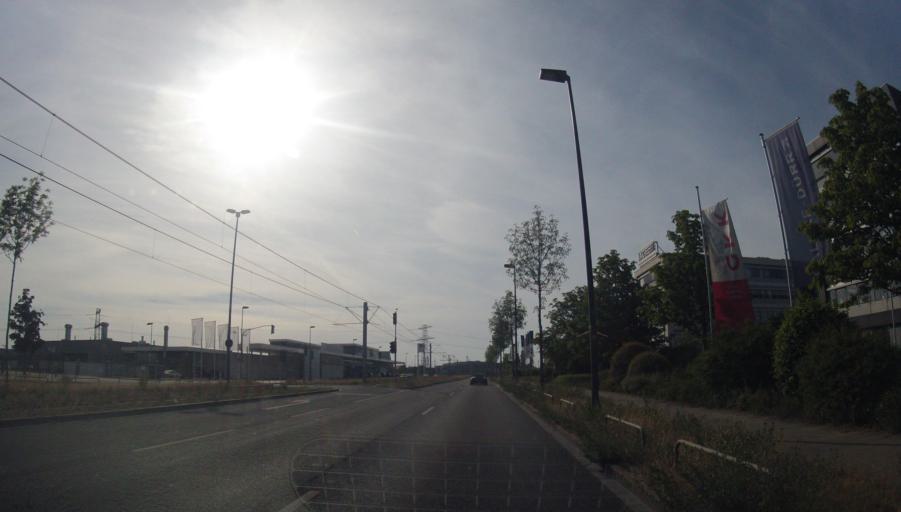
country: DE
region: North Rhine-Westphalia
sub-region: Regierungsbezirk Dusseldorf
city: Ratingen
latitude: 51.2733
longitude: 6.8115
